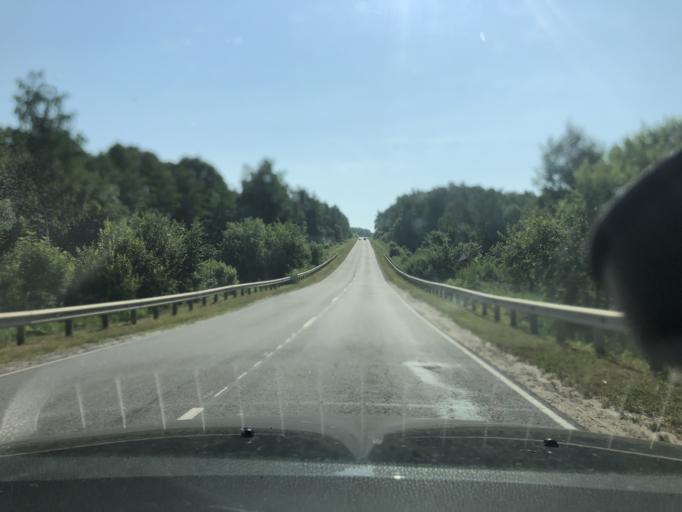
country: RU
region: Tula
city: Dubna
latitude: 54.1299
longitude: 37.0456
